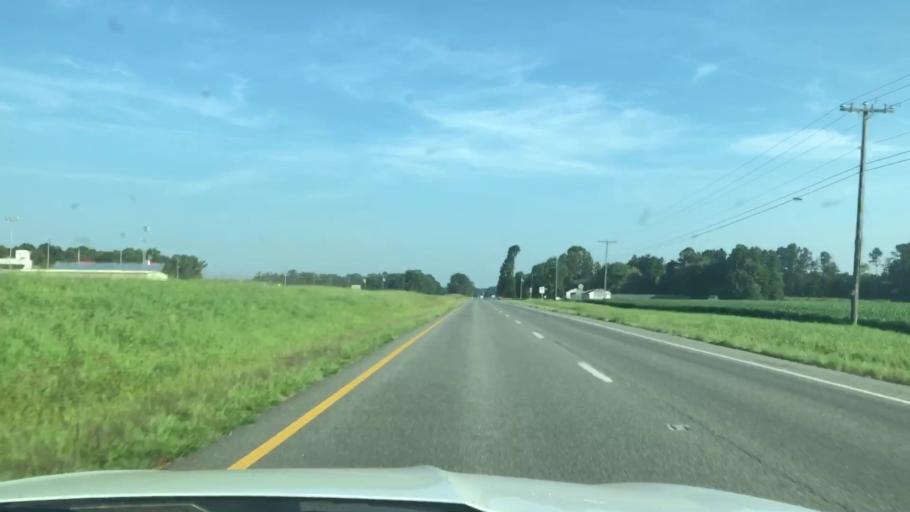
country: US
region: Virginia
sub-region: Middlesex County
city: Saluda
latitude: 37.7030
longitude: -76.6881
